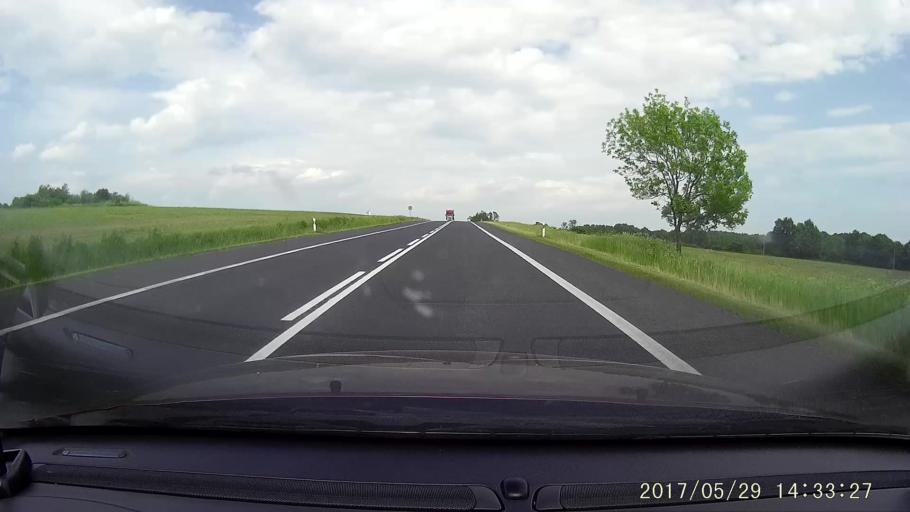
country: PL
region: Lower Silesian Voivodeship
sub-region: Powiat zgorzelecki
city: Lagow
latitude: 51.2006
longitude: 15.0986
